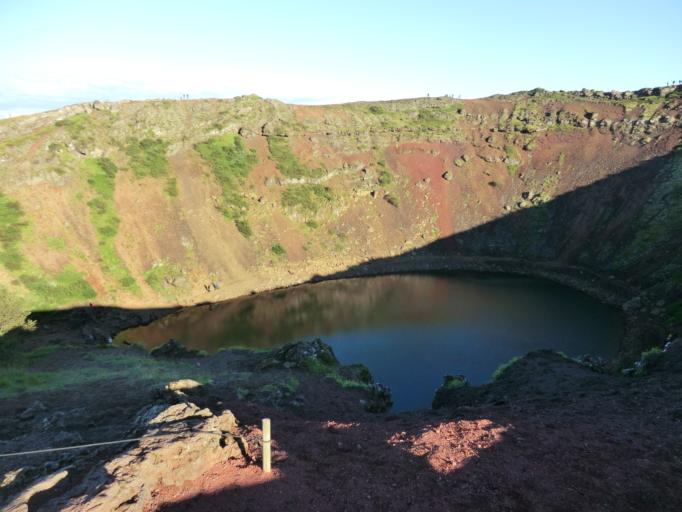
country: IS
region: South
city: Selfoss
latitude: 64.0416
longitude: -20.8860
